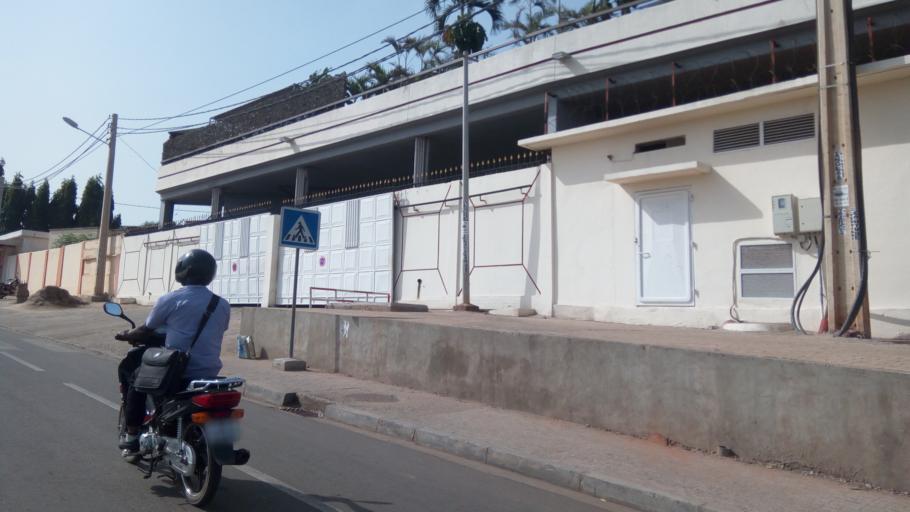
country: TG
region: Maritime
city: Lome
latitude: 6.1417
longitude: 1.2085
